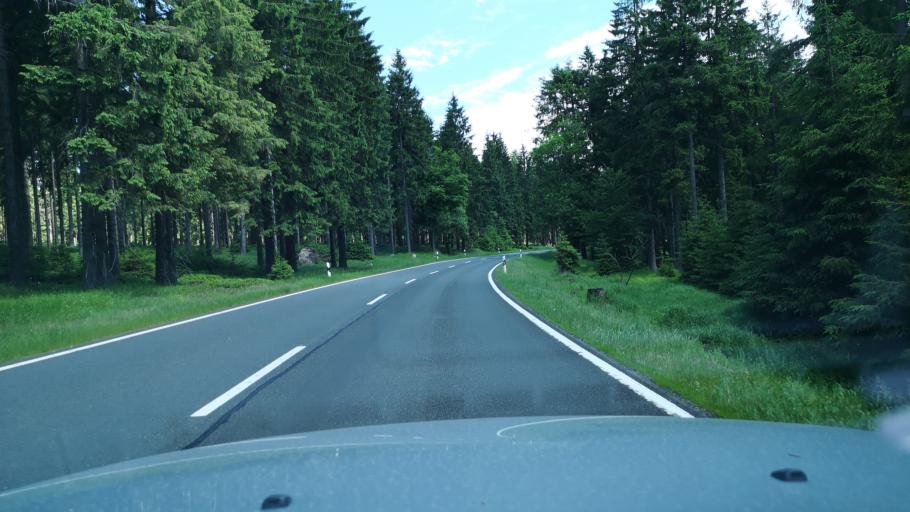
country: DE
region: Thuringia
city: Neuhaus am Rennweg
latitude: 50.4954
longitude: 11.1051
